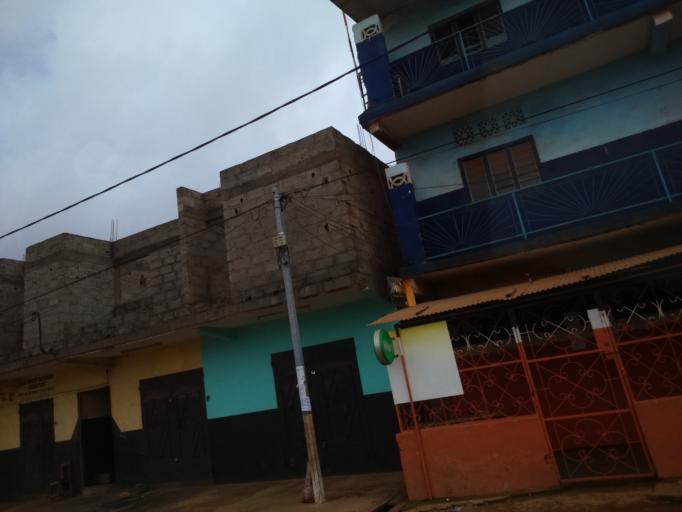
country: CI
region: Moyen-Comoe
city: Abengourou
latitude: 6.7266
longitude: -3.4992
